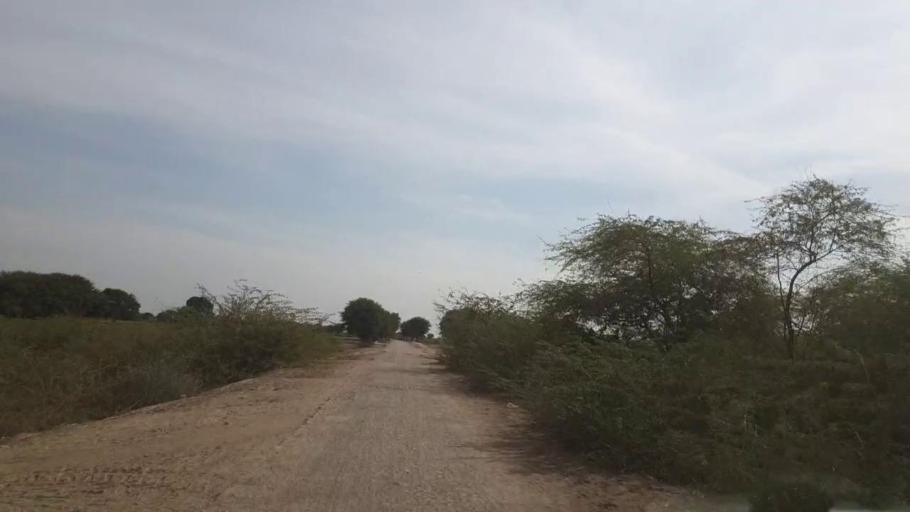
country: PK
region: Sindh
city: Nabisar
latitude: 25.0286
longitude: 69.5624
